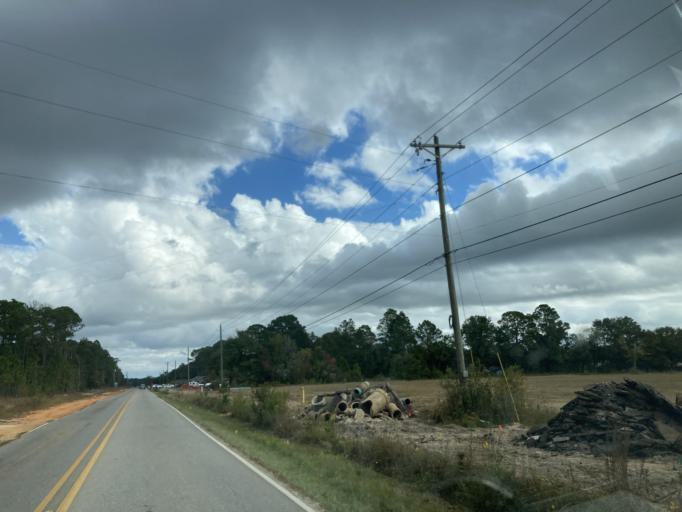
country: US
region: Mississippi
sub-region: Jackson County
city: Gulf Hills
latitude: 30.4391
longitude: -88.8294
